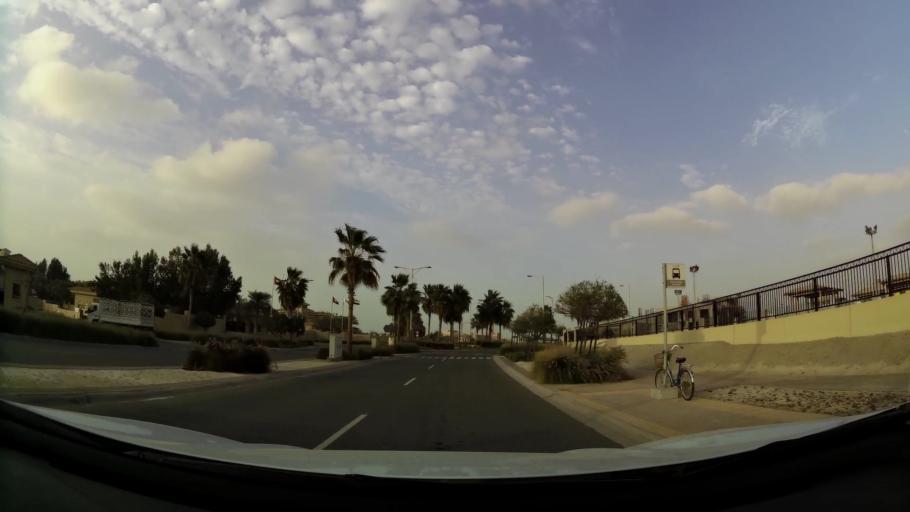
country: AE
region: Abu Dhabi
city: Abu Dhabi
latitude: 24.5364
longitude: 54.4281
